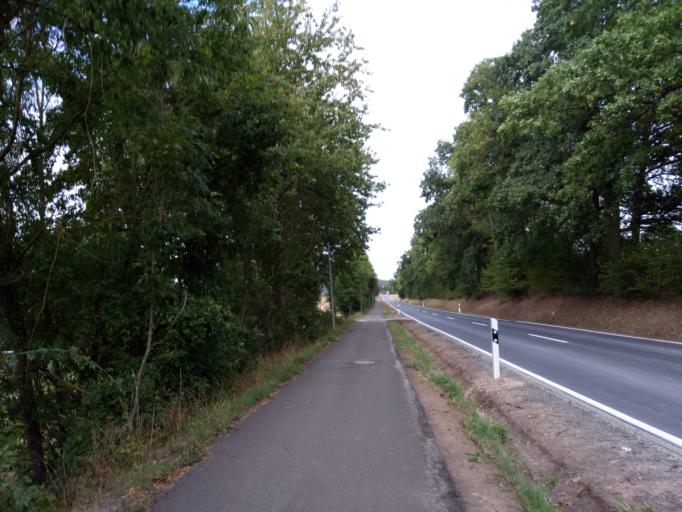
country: DE
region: Rheinland-Pfalz
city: Waldlaubersheim
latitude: 49.9402
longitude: 7.8208
